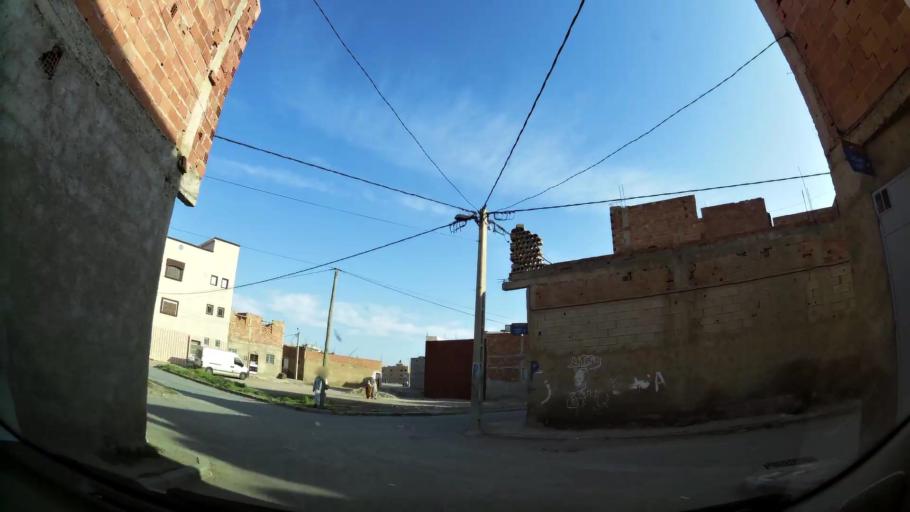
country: MA
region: Oriental
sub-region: Oujda-Angad
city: Oujda
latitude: 34.7150
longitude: -1.8971
